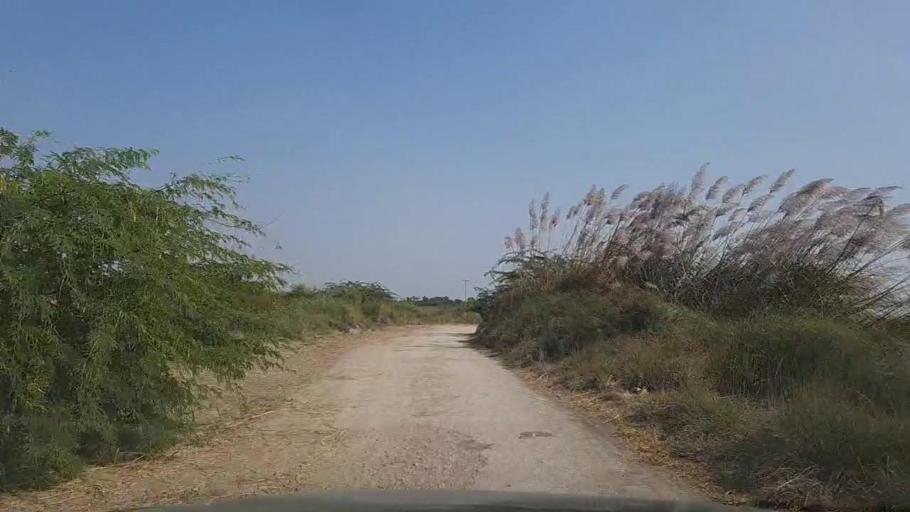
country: PK
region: Sindh
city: Thatta
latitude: 24.5986
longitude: 67.9531
